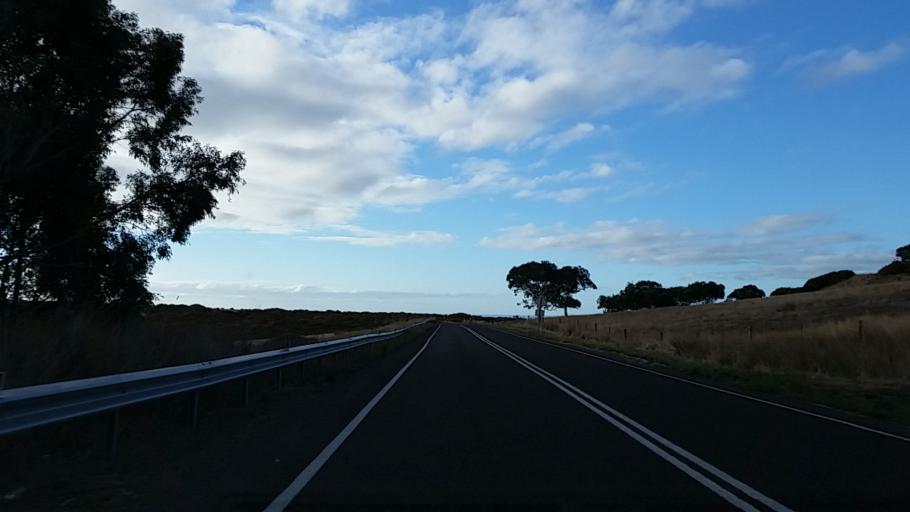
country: AU
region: South Australia
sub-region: Yankalilla
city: Normanville
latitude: -35.5584
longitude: 138.1983
